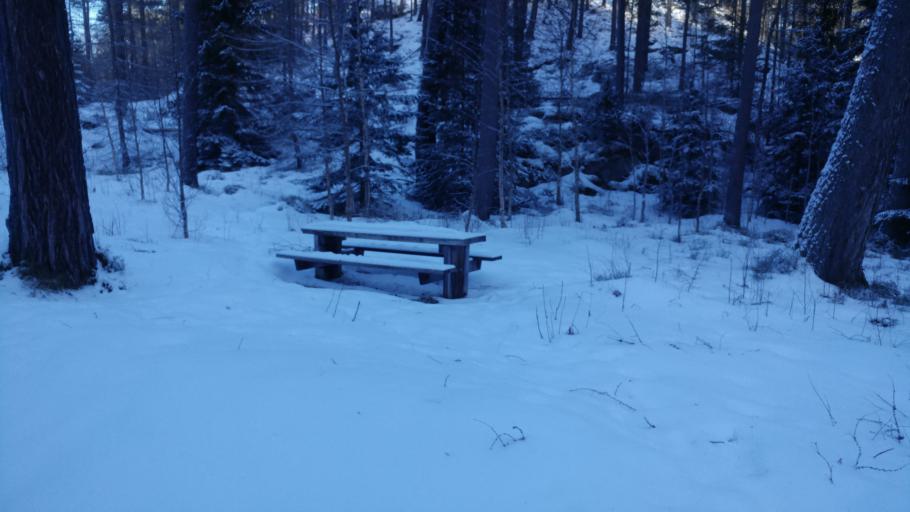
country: NO
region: Sor-Trondelag
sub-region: Trondheim
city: Trondheim
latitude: 63.4383
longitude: 10.3378
